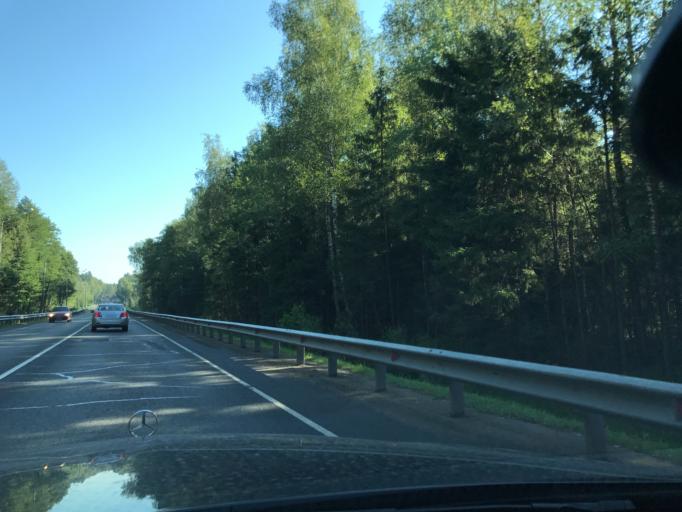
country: RU
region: Moskovskaya
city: Losino-Petrovskiy
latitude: 55.9328
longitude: 38.2108
